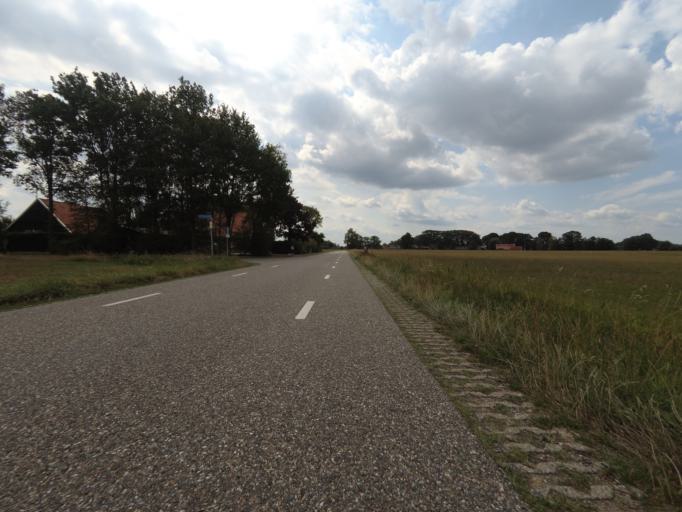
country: NL
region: Overijssel
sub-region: Gemeente Hof van Twente
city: Hengevelde
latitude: 52.1634
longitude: 6.6809
